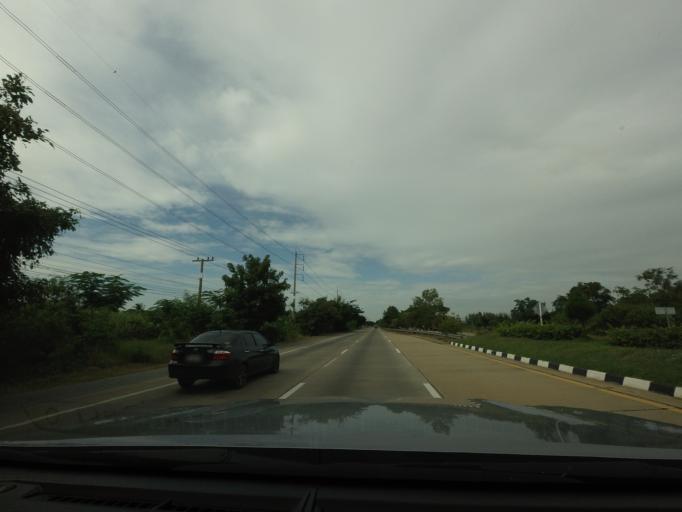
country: TH
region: Suphan Buri
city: Doem Bang Nang Buat
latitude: 14.8711
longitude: 100.0870
